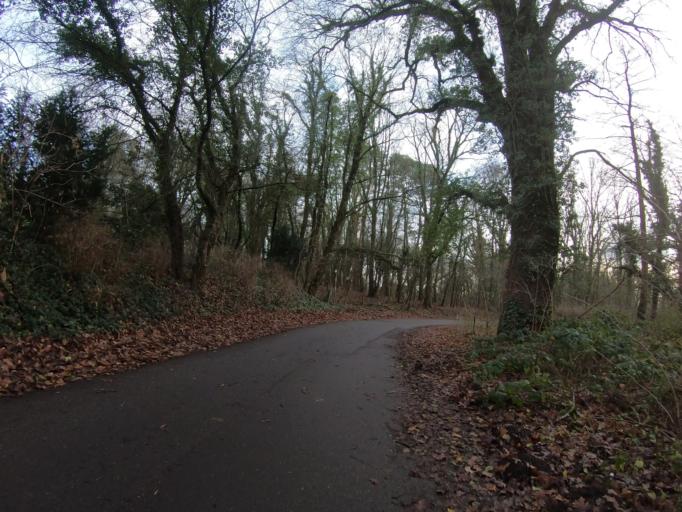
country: DE
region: Lower Saxony
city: Gifhorn
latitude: 52.4887
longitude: 10.5211
